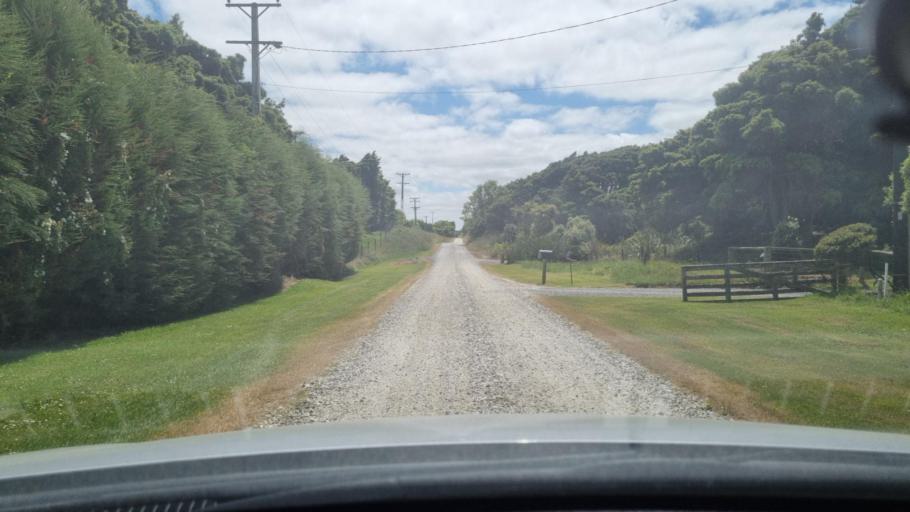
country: NZ
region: Southland
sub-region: Invercargill City
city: Invercargill
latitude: -46.4562
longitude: 168.2813
